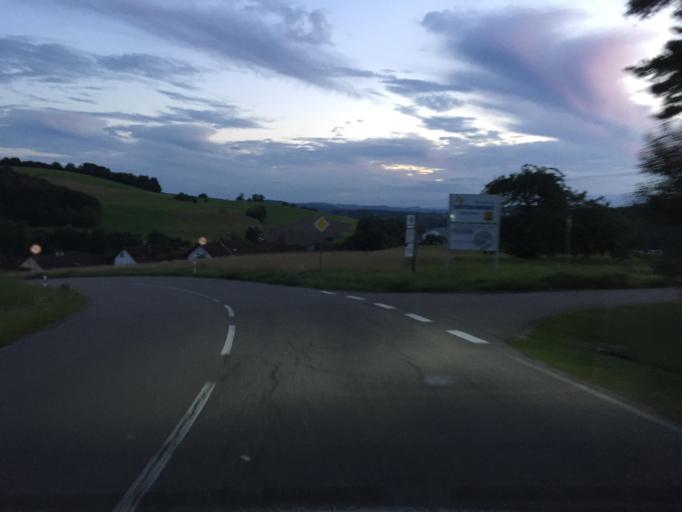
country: DE
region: Baden-Wuerttemberg
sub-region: Freiburg Region
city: Wutoschingen
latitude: 47.6691
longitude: 8.3867
